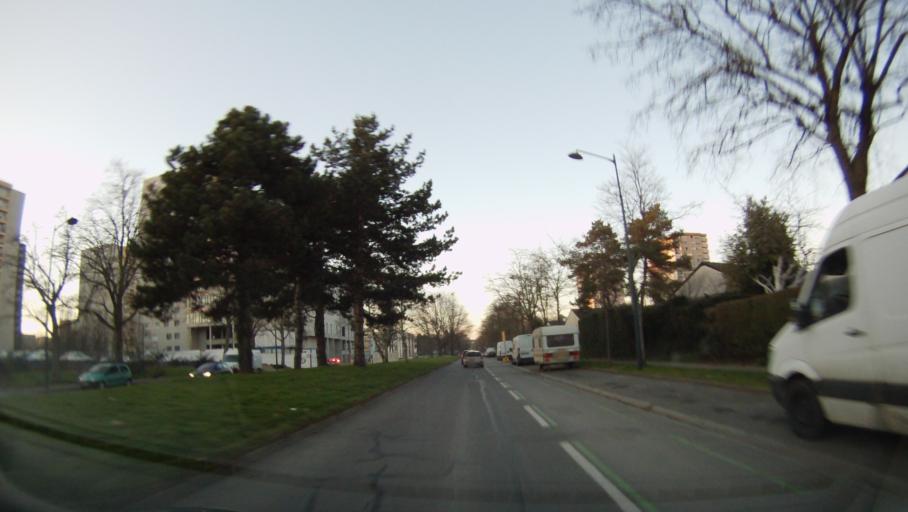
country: FR
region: Brittany
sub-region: Departement d'Ille-et-Vilaine
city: Rennes
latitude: 48.0860
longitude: -1.6509
